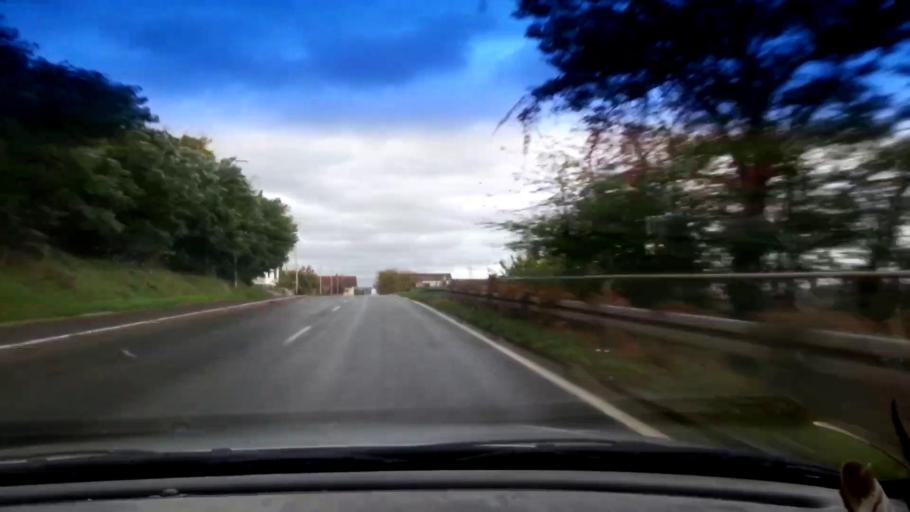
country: DE
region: Bavaria
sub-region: Upper Franconia
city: Hallstadt
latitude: 49.9320
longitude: 10.8539
